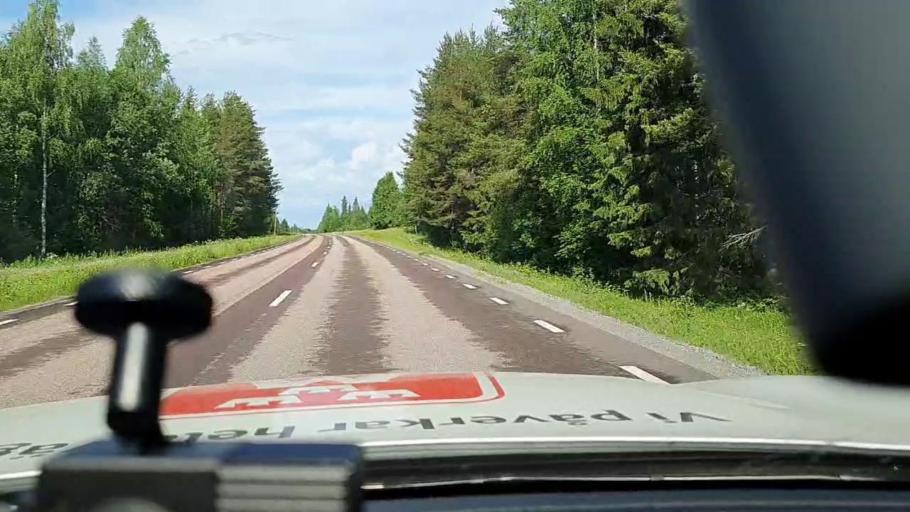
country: SE
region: Norrbotten
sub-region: Alvsbyns Kommun
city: AElvsbyn
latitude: 66.0222
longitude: 21.1295
